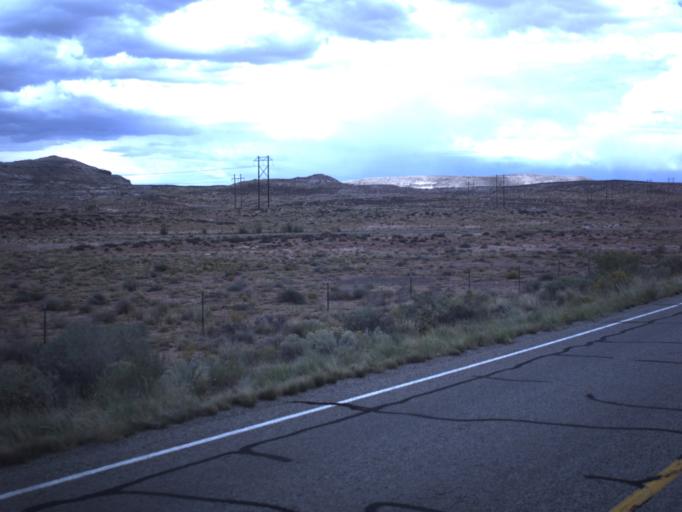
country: US
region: Utah
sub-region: San Juan County
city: Blanding
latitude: 37.2884
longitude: -109.3966
